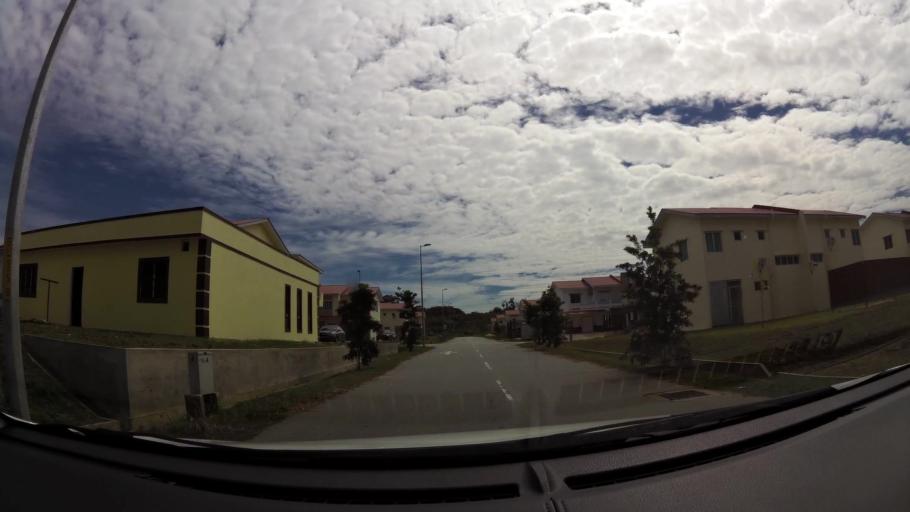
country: BN
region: Brunei and Muara
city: Bandar Seri Begawan
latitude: 4.9785
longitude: 115.0019
